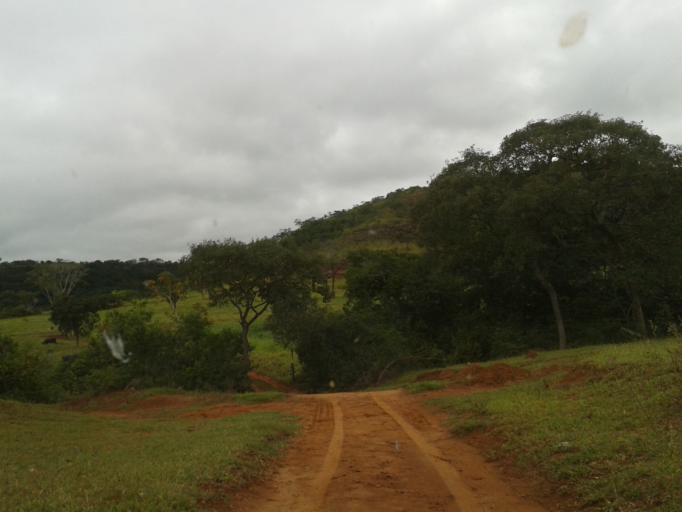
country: BR
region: Minas Gerais
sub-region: Campina Verde
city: Campina Verde
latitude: -19.4676
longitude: -49.5818
